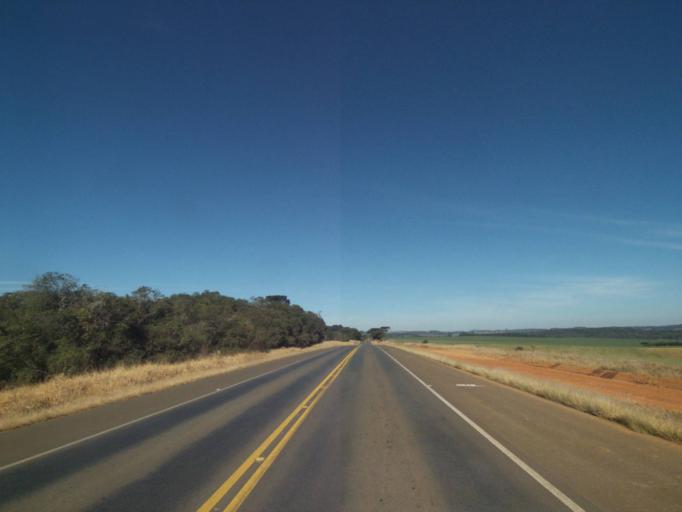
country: BR
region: Parana
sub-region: Tibagi
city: Tibagi
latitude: -24.6988
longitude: -50.4464
